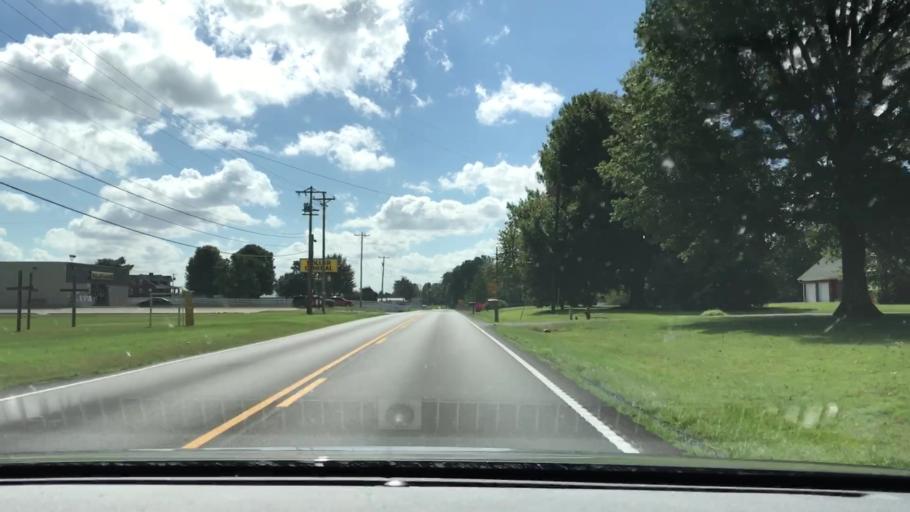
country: US
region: Kentucky
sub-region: Graves County
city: Mayfield
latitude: 36.7639
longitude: -88.5961
